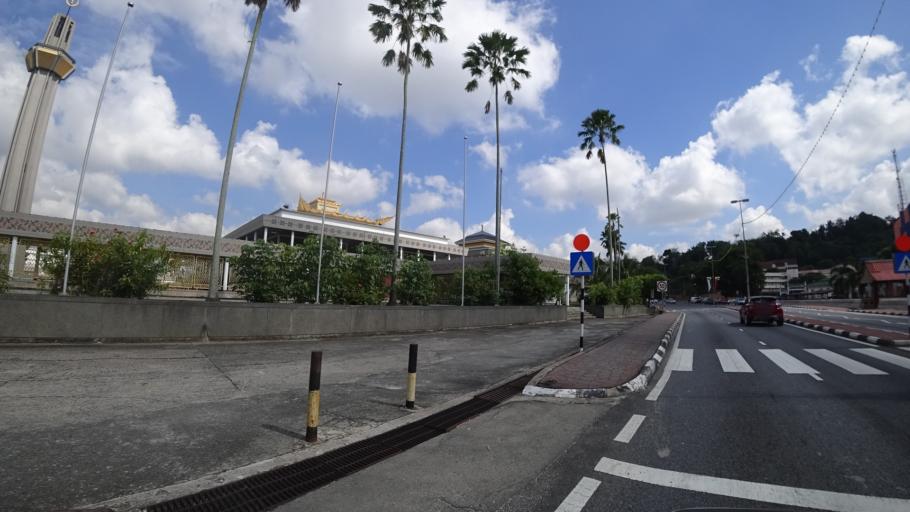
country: BN
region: Brunei and Muara
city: Bandar Seri Begawan
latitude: 4.8922
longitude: 114.9436
